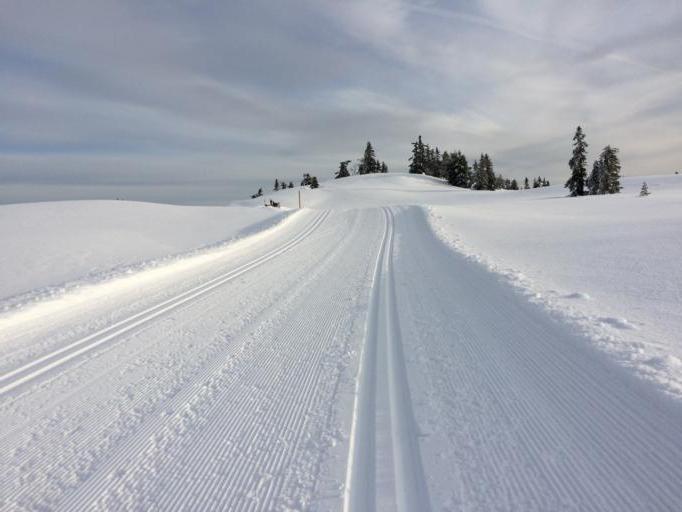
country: NO
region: Oppland
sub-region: Gausdal
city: Segalstad bru
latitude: 61.3252
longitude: 10.0394
